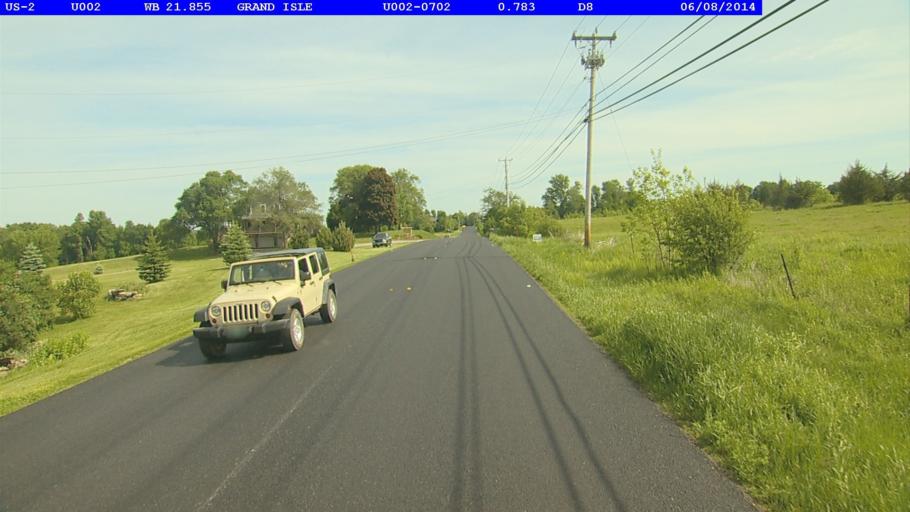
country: US
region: Vermont
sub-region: Grand Isle County
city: North Hero
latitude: 44.7560
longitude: -73.2865
